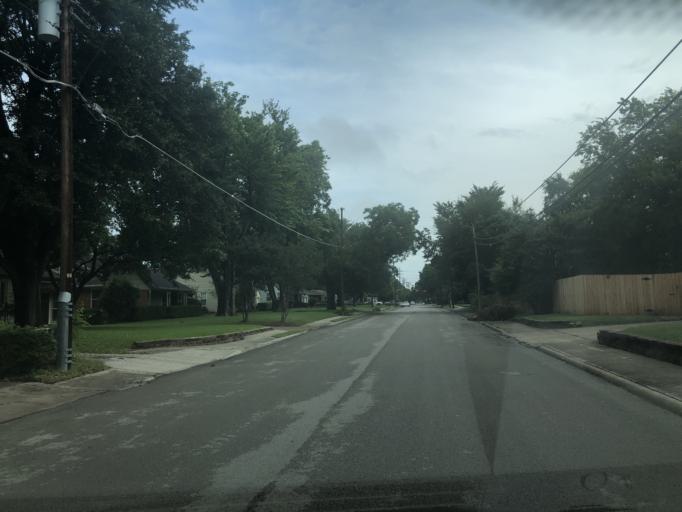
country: US
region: Texas
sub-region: Dallas County
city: Irving
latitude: 32.8066
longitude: -96.9424
